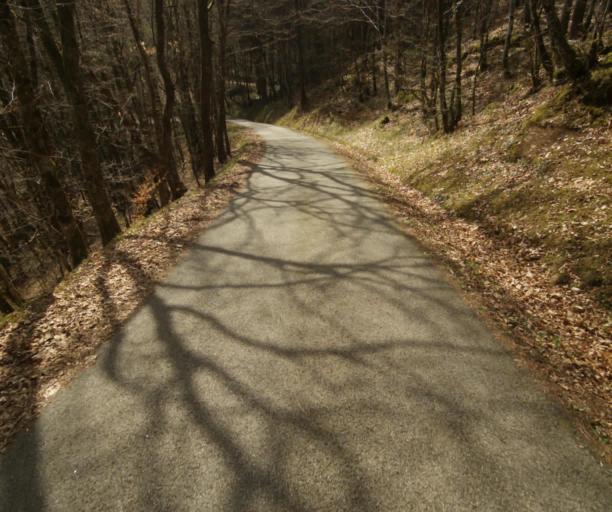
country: FR
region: Limousin
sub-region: Departement de la Correze
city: Naves
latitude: 45.3469
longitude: 1.8025
